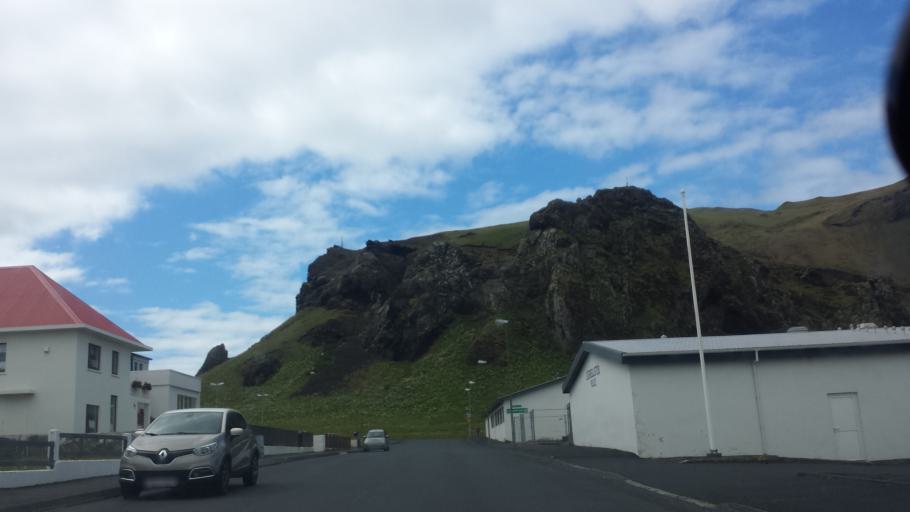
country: IS
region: South
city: Vestmannaeyjar
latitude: 63.4405
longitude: -20.2791
